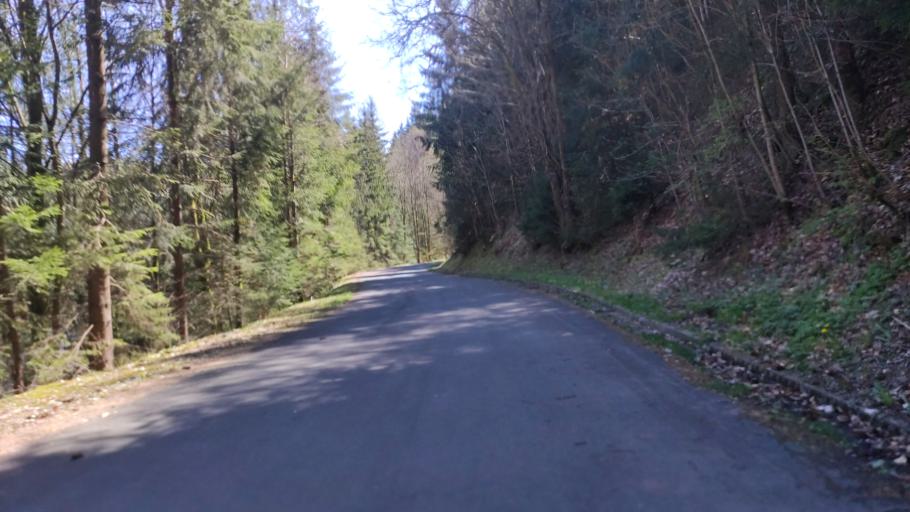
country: DE
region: Bavaria
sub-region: Upper Franconia
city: Nordhalben
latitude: 50.3585
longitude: 11.4844
